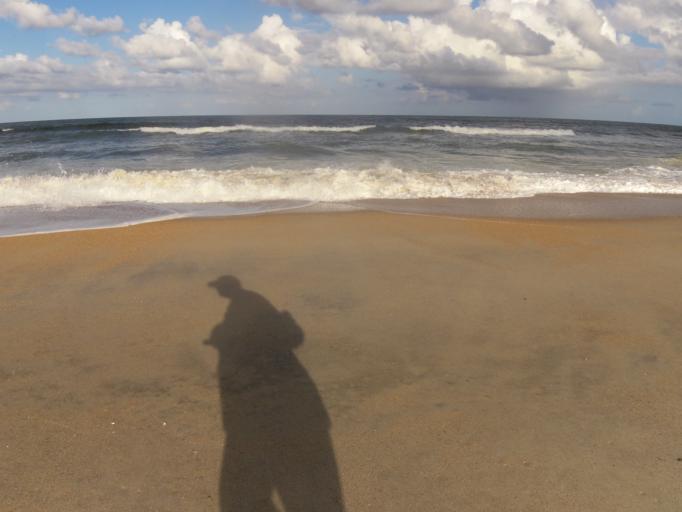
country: US
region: Florida
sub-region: Saint Johns County
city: Palm Valley
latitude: 30.0910
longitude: -81.3384
